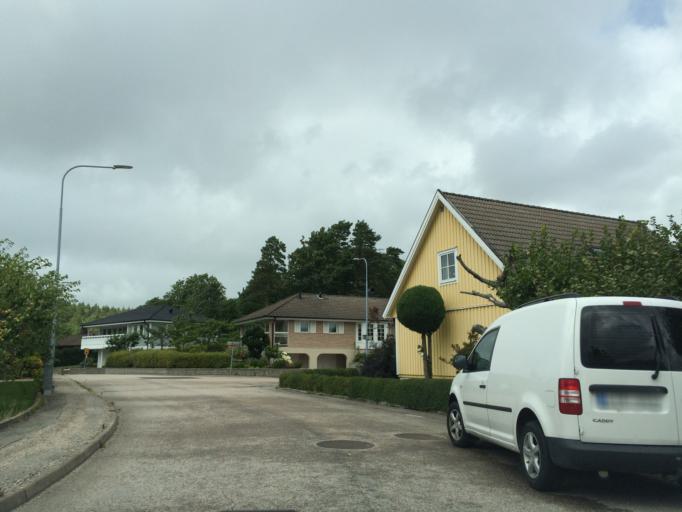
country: SE
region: Vaestra Goetaland
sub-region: Trollhattan
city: Trollhattan
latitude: 58.2927
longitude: 12.2774
